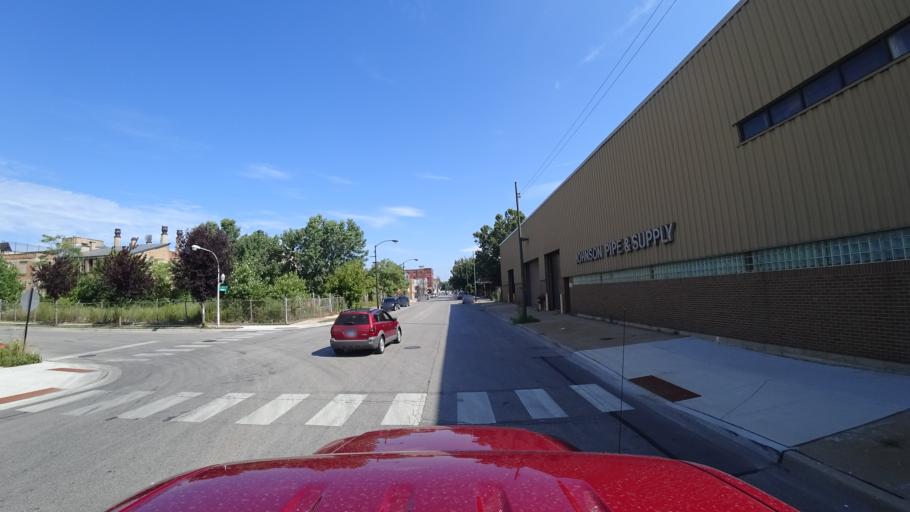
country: US
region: Illinois
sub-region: Cook County
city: Chicago
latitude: 41.8269
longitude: -87.6508
